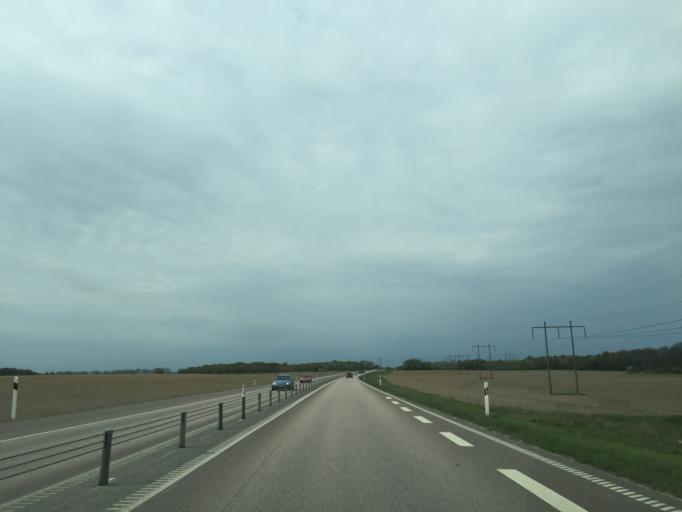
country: SE
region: Skane
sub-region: Helsingborg
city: Odakra
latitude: 56.0933
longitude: 12.6942
